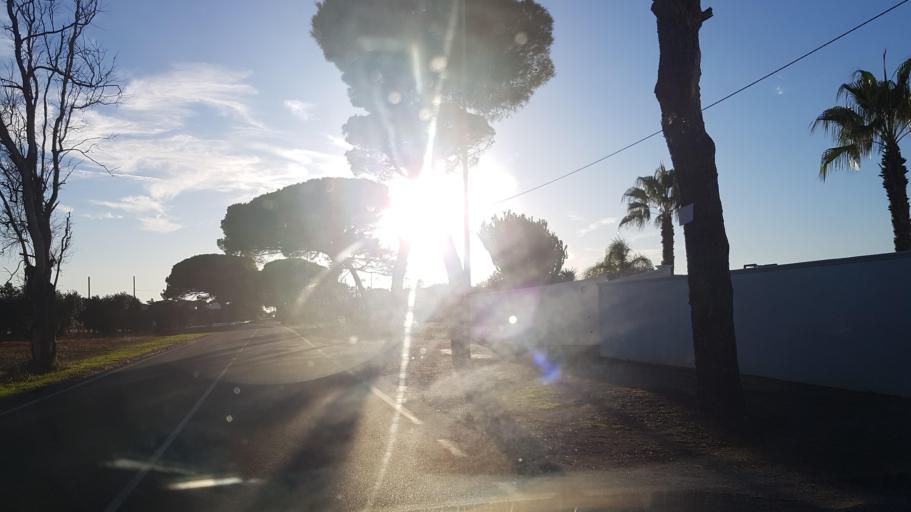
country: IT
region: Apulia
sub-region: Provincia di Lecce
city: Giorgilorio
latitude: 40.4199
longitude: 18.2253
